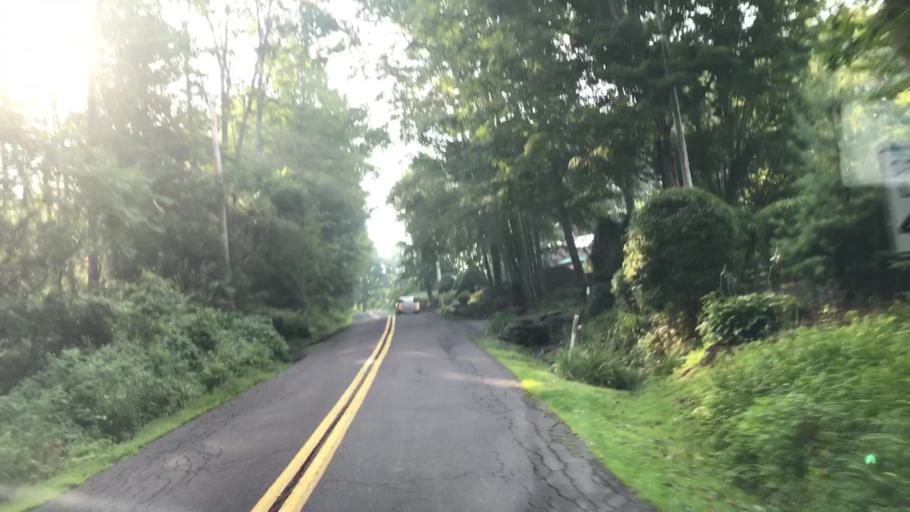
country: US
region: Pennsylvania
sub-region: Wyoming County
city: Factoryville
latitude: 41.6171
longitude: -75.7491
